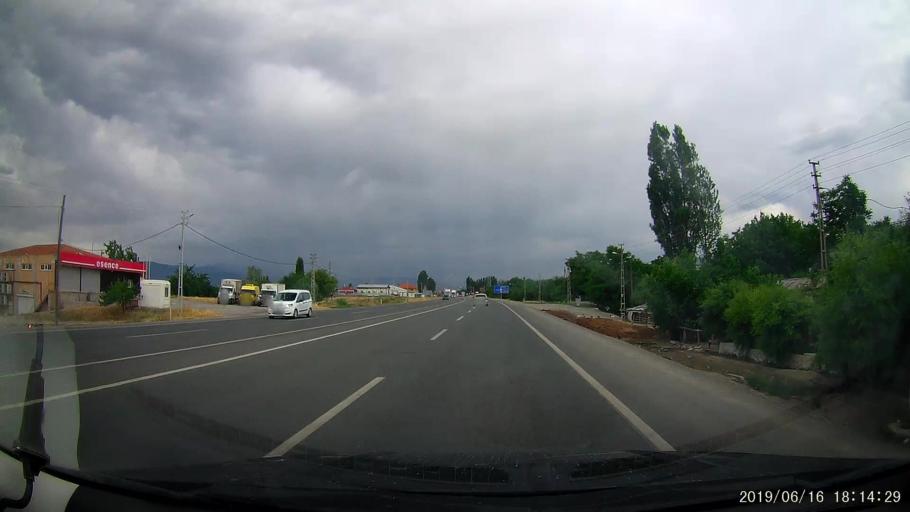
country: TR
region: Erzincan
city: Erzincan
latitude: 39.7243
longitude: 39.5575
